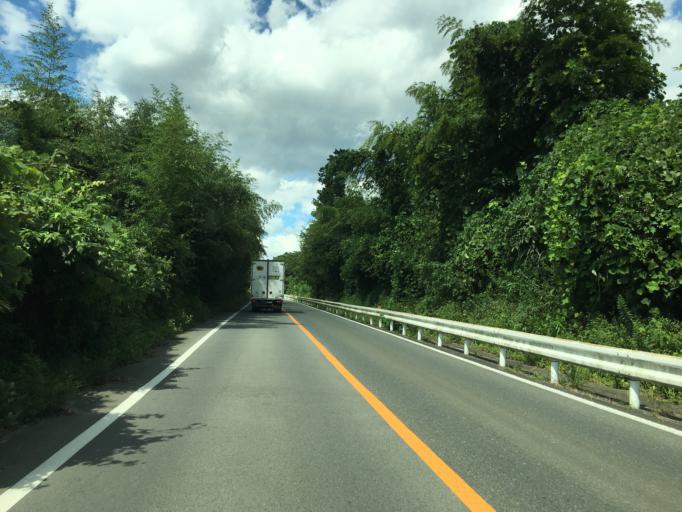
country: JP
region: Fukushima
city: Namie
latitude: 37.3463
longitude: 141.0009
